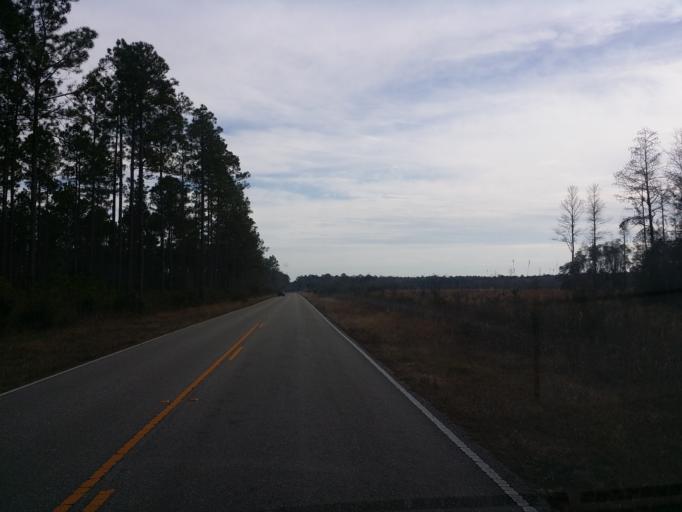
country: US
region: Florida
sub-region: Leon County
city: Woodville
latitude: 30.1717
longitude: -84.1600
